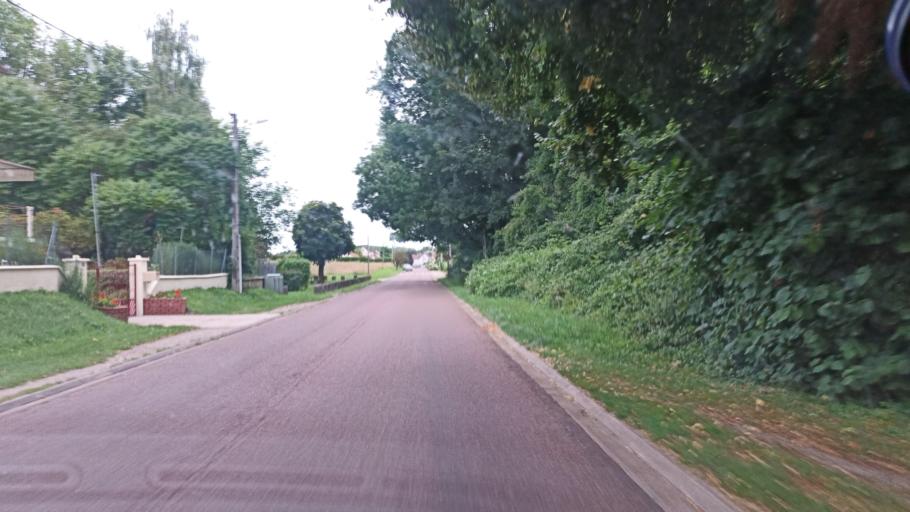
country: FR
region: Ile-de-France
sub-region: Departement de Seine-et-Marne
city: Voulx
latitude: 48.2787
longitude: 2.9776
